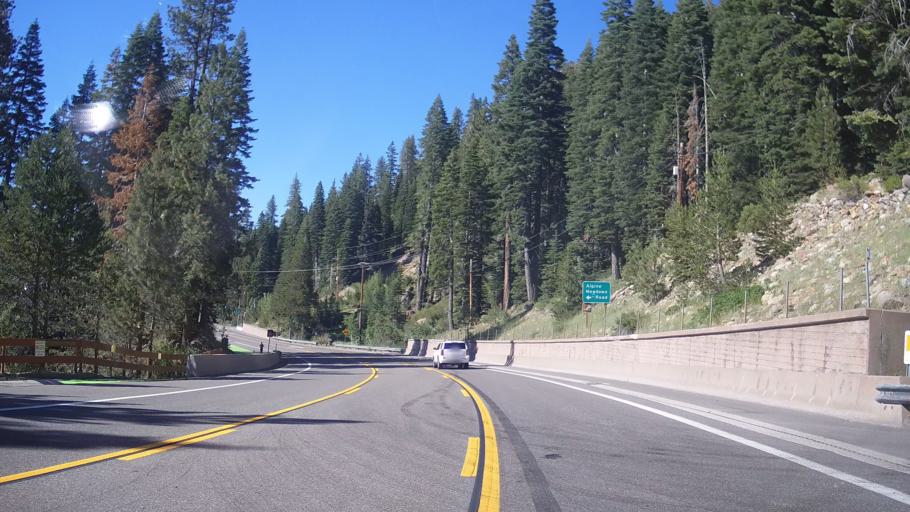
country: US
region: California
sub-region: Placer County
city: Sunnyside-Tahoe City
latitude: 39.1849
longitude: -120.1947
